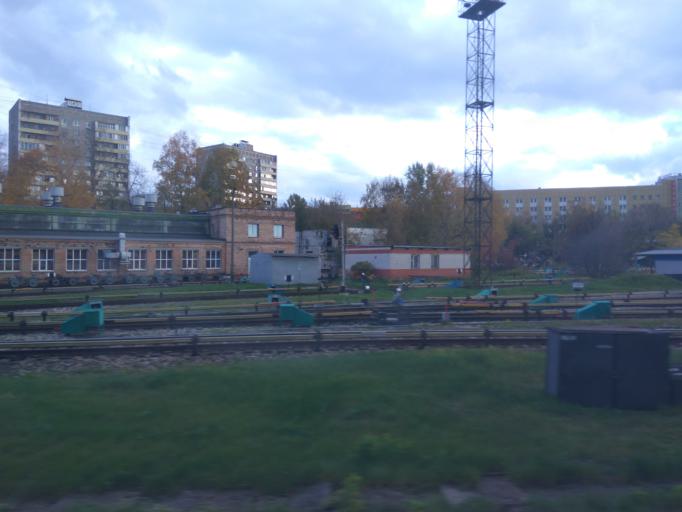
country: RU
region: Moskovskaya
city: Fili
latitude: 55.7459
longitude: 37.5041
